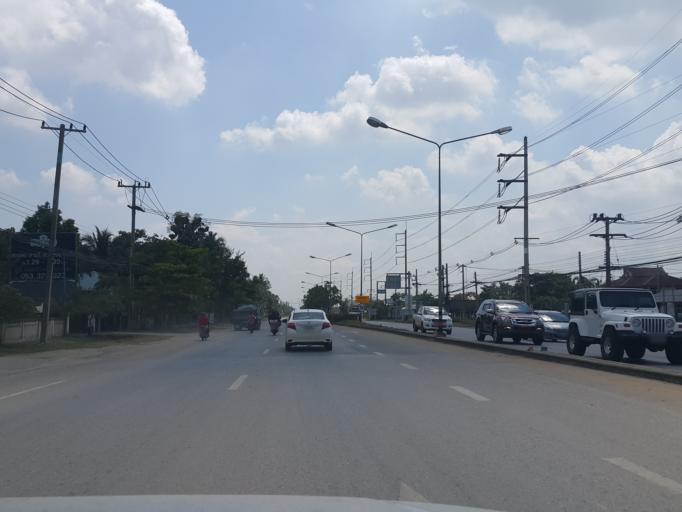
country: TH
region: Chiang Mai
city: San Sai
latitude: 18.9216
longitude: 98.9946
